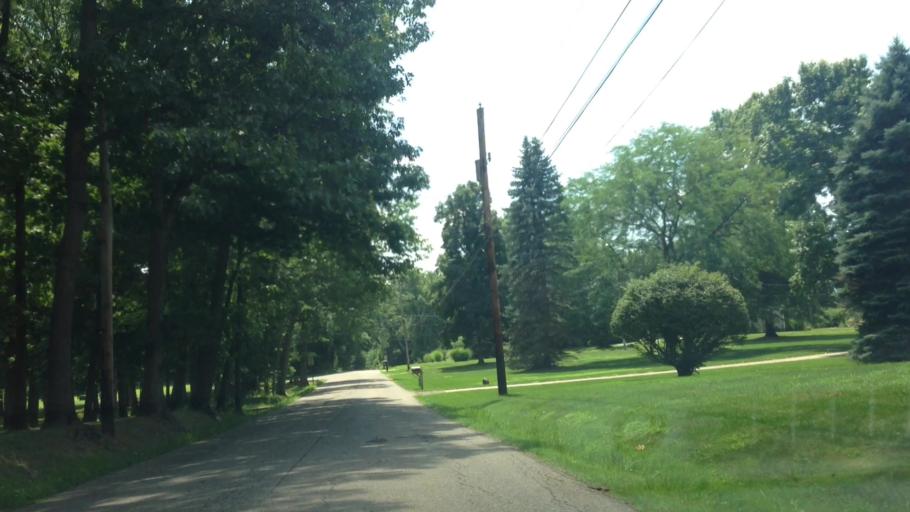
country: US
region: Ohio
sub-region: Summit County
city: Clinton
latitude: 40.9592
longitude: -81.6476
